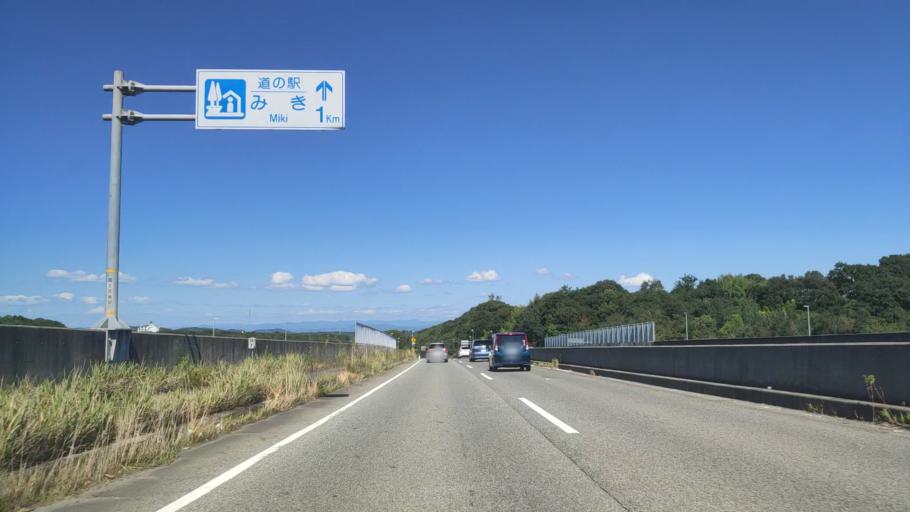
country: JP
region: Hyogo
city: Miki
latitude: 34.7795
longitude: 134.9827
